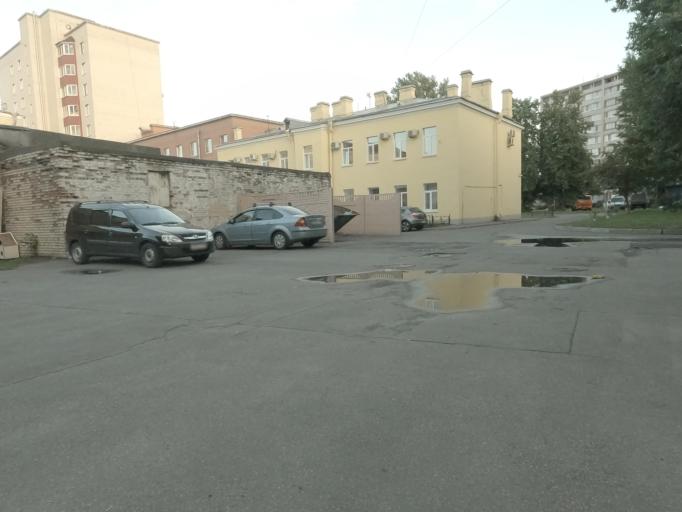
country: RU
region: St.-Petersburg
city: Avtovo
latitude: 59.8934
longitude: 30.2659
